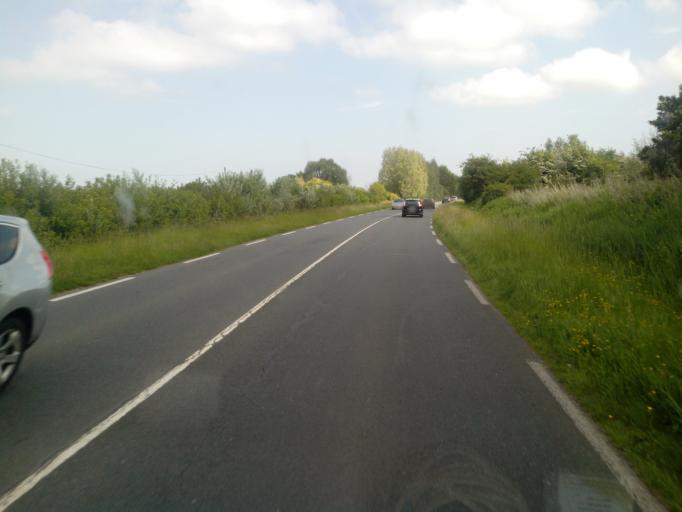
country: FR
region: Picardie
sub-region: Departement de la Somme
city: Saint-Valery-sur-Somme
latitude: 50.1960
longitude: 1.6960
